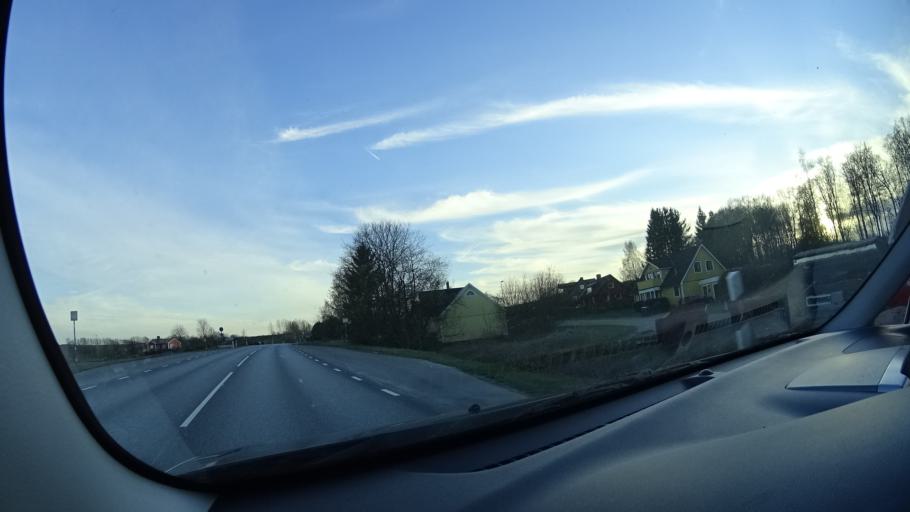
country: SE
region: Skane
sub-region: Eslovs Kommun
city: Stehag
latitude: 55.9251
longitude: 13.3755
